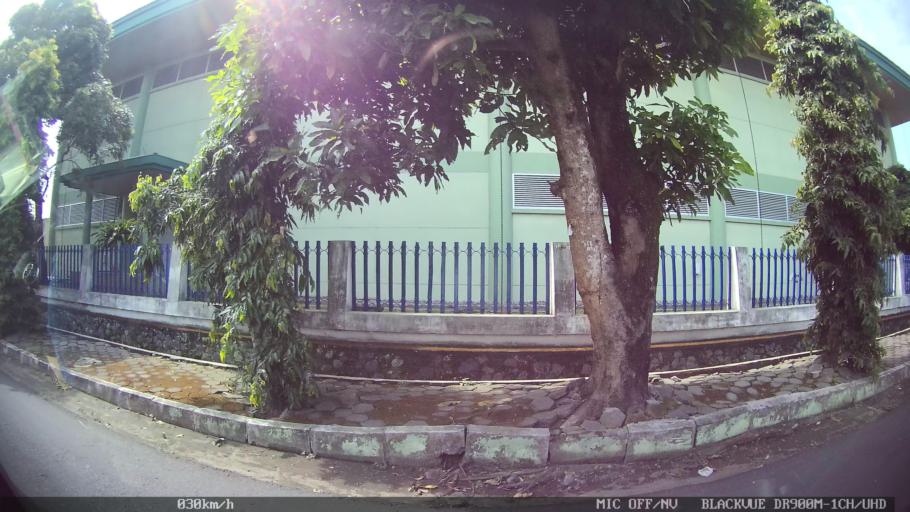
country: ID
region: Daerah Istimewa Yogyakarta
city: Depok
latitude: -7.7604
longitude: 110.4282
